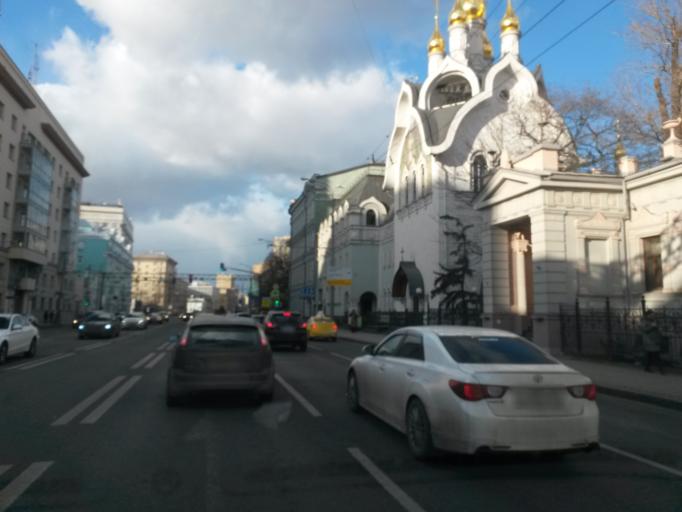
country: RU
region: Moscow
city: Mar'ina Roshcha
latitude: 55.7764
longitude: 37.6325
